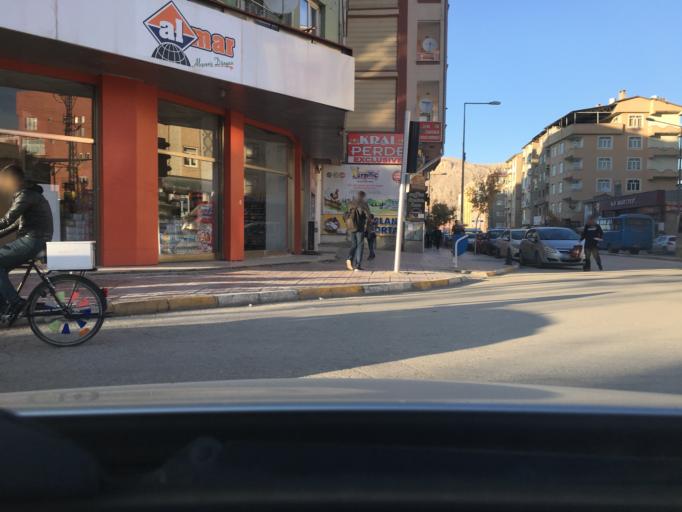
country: TR
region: Van
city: Van
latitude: 38.4981
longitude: 43.3991
